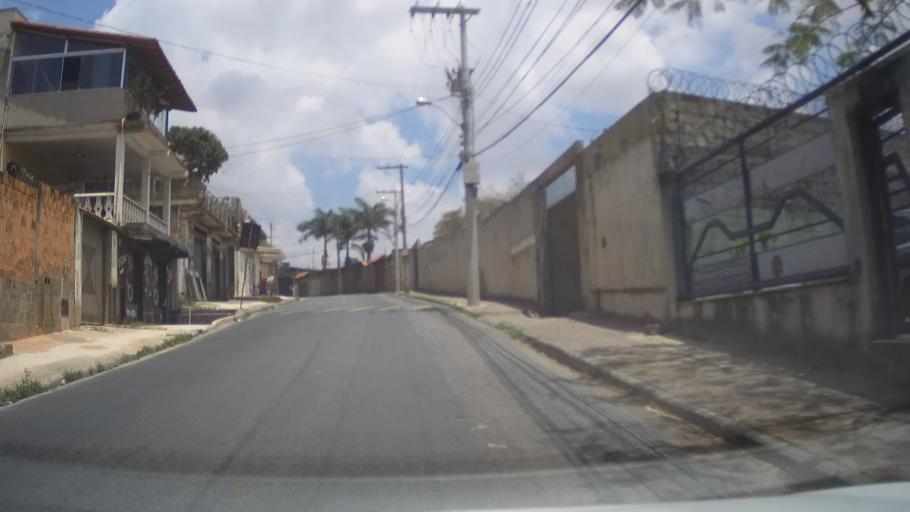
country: BR
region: Minas Gerais
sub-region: Belo Horizonte
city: Belo Horizonte
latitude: -19.9036
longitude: -43.8825
